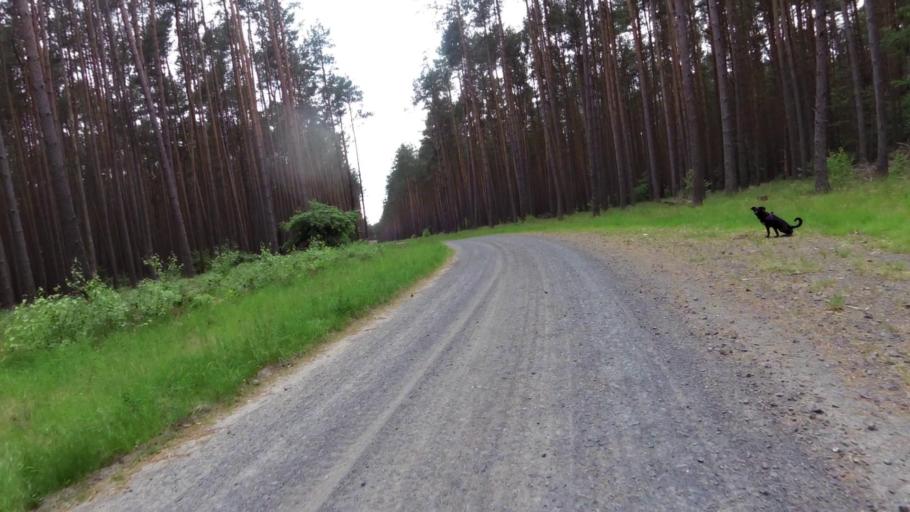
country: PL
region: West Pomeranian Voivodeship
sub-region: Powiat mysliborski
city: Debno
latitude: 52.8300
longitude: 14.6410
